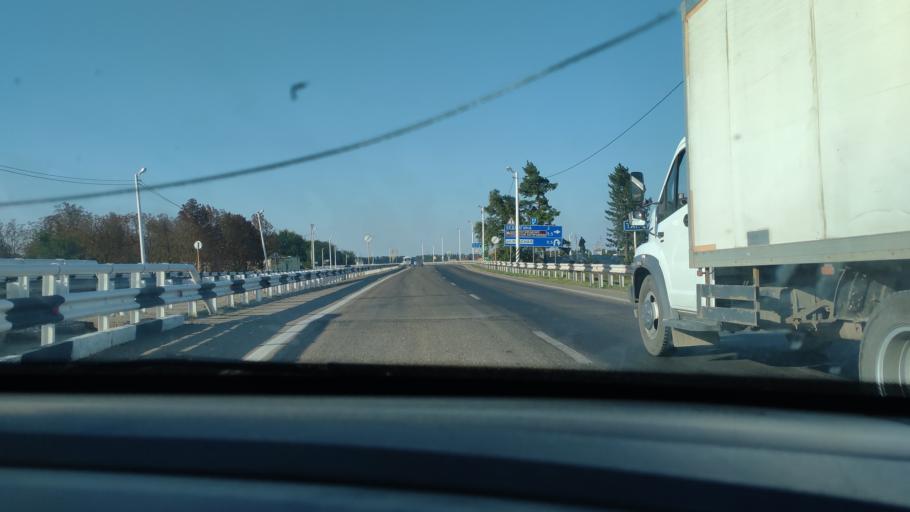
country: RU
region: Krasnodarskiy
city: Timashevsk
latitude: 45.5192
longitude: 38.9412
